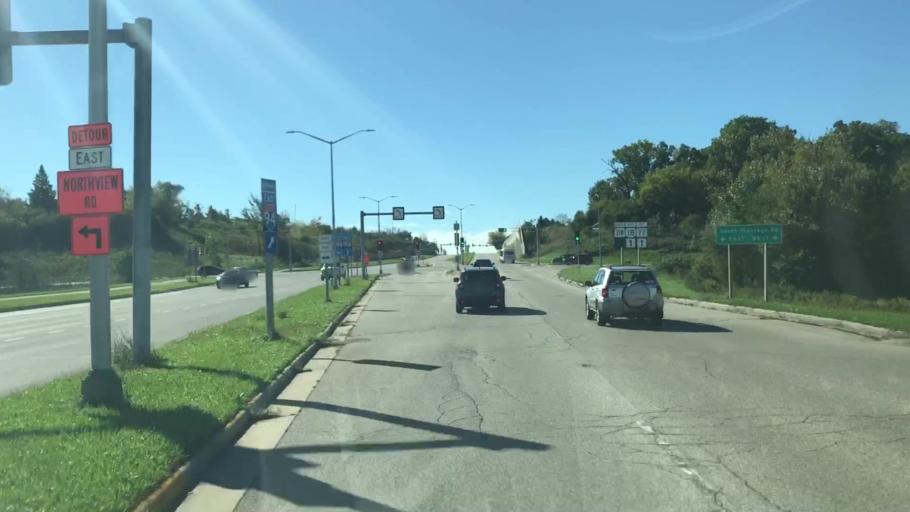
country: US
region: Wisconsin
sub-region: Waukesha County
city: Pewaukee
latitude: 43.0485
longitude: -88.2858
